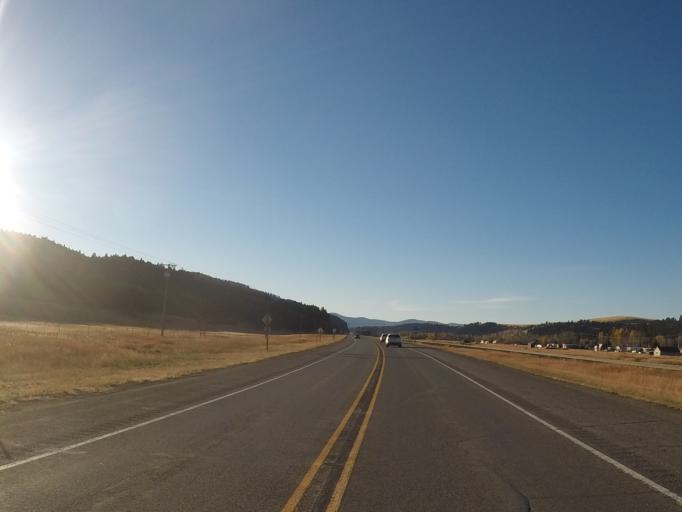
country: US
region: Montana
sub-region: Lewis and Clark County
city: Helena West Side
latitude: 46.5616
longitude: -112.4318
